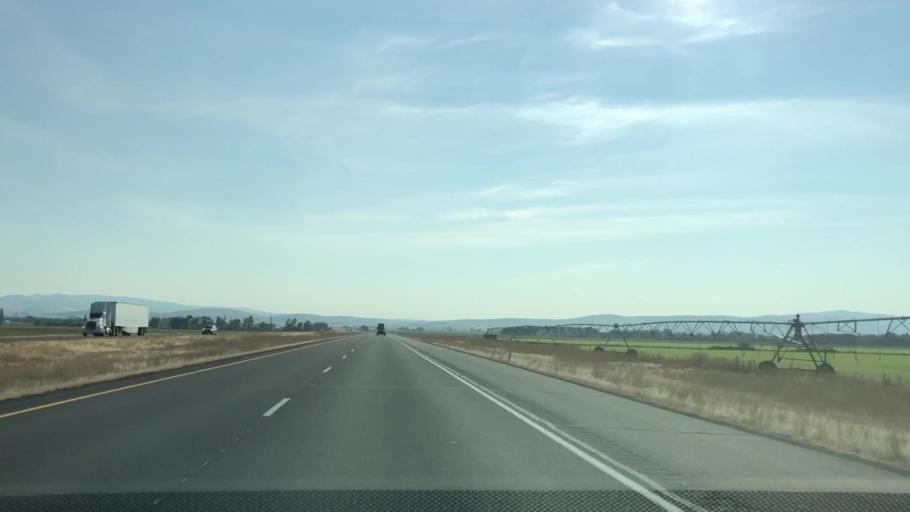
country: US
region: Washington
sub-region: Kittitas County
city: Kittitas
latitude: 46.9700
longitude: -120.4654
